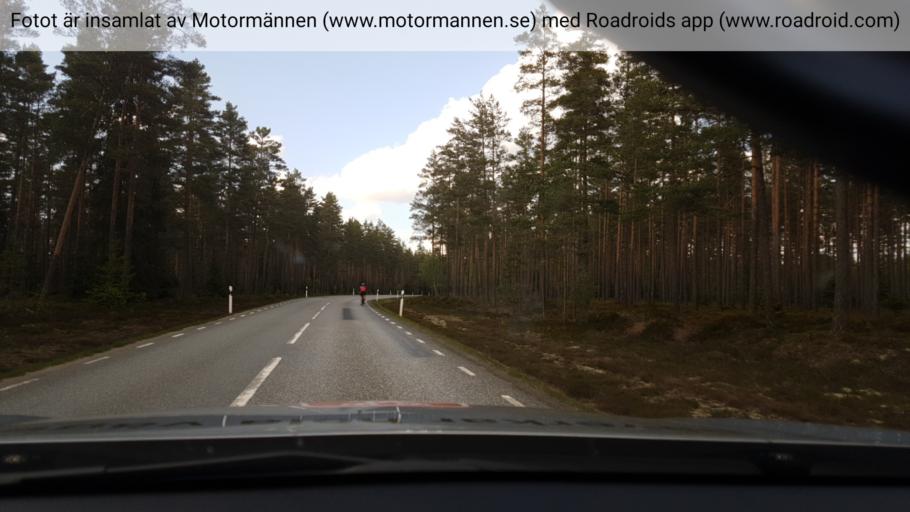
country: SE
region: Joenkoeping
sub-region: Gnosjo Kommun
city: Hillerstorp
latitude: 57.3782
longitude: 13.9730
